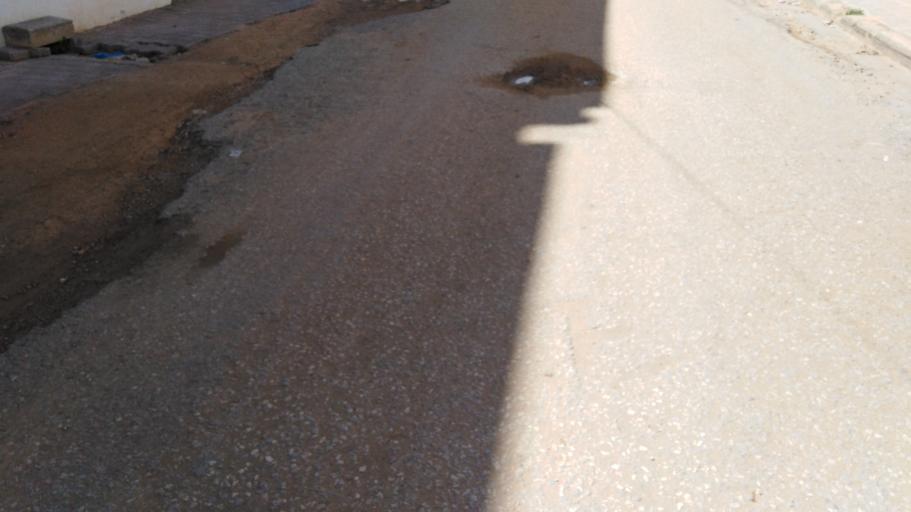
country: TN
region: Safaqis
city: Sfax
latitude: 34.7428
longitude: 10.5287
